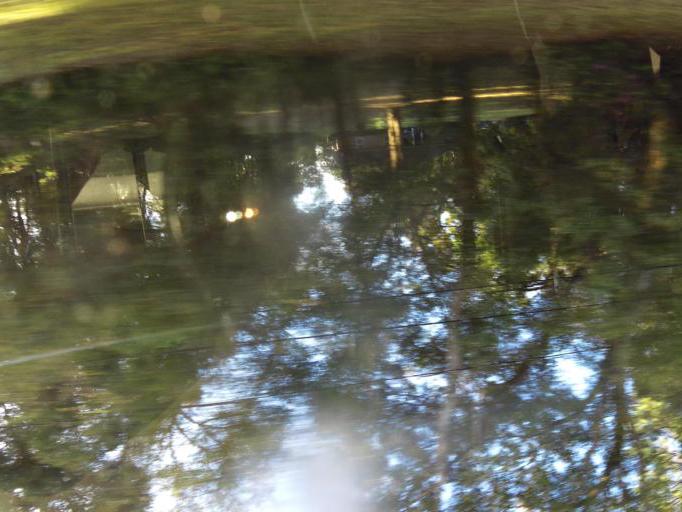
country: US
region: Florida
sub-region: Duval County
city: Jacksonville
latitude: 30.4398
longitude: -81.6158
